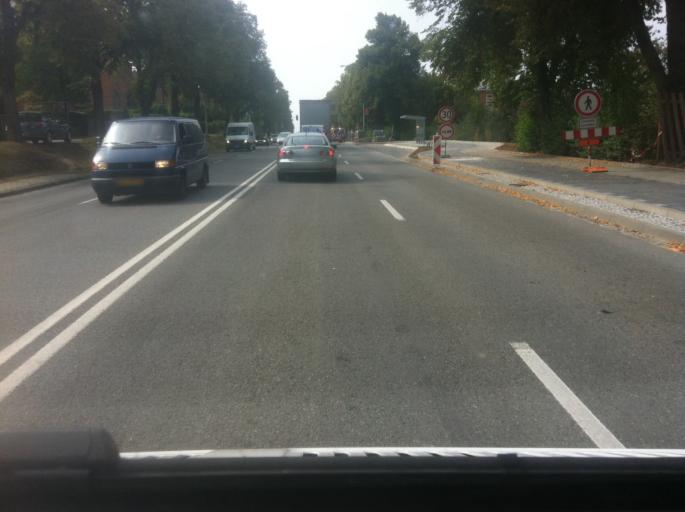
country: CZ
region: Zlin
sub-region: Okres Zlin
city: Zlin
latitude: 49.2254
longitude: 17.6840
